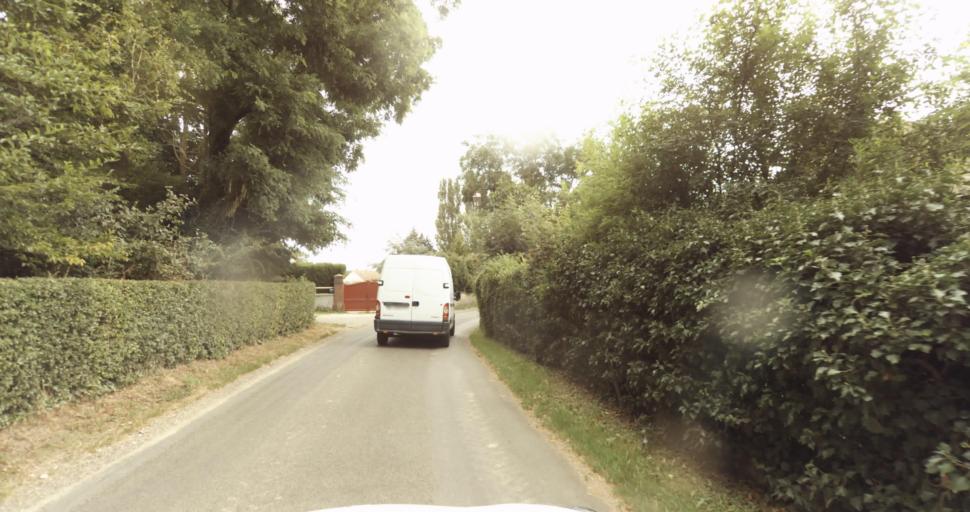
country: FR
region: Centre
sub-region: Departement d'Eure-et-Loir
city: Saint-Remy-sur-Avre
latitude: 48.8144
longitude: 1.2408
